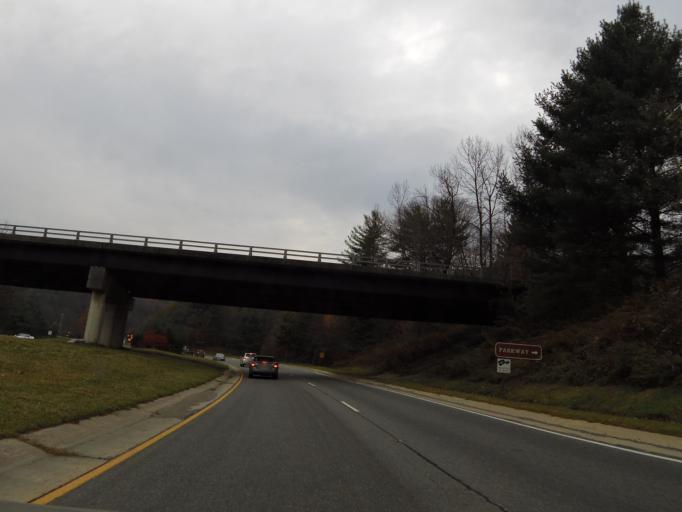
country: US
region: North Carolina
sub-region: Watauga County
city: Blowing Rock
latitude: 36.1483
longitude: -81.6625
